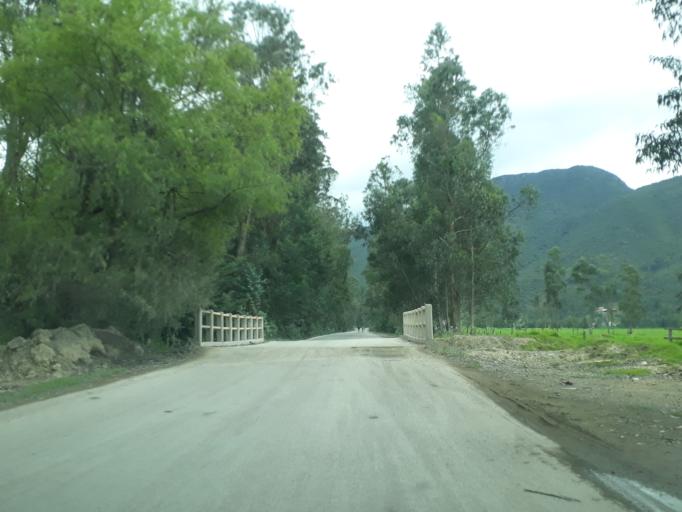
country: CO
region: Cundinamarca
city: Lenguazaque
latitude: 5.3260
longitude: -73.7496
